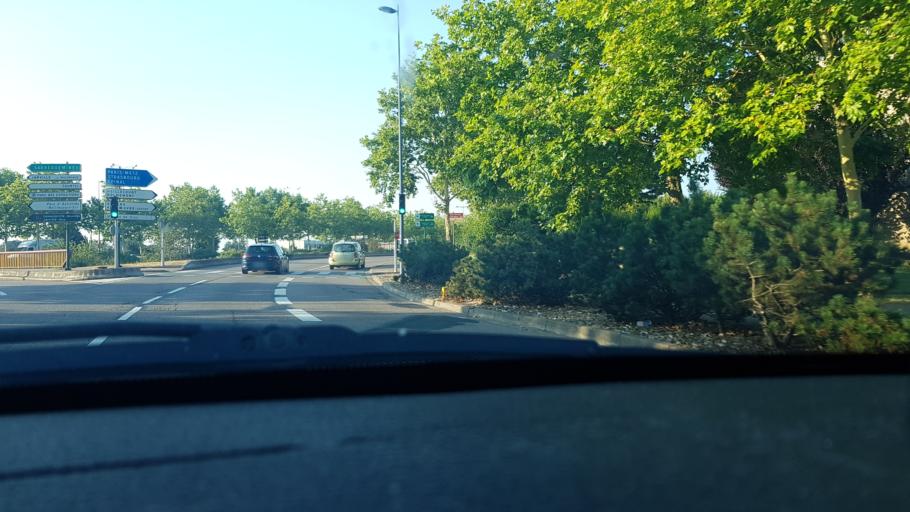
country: FR
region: Lorraine
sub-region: Departement de Meurthe-et-Moselle
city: Jarville-la-Malgrange
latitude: 48.6674
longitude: 6.1902
